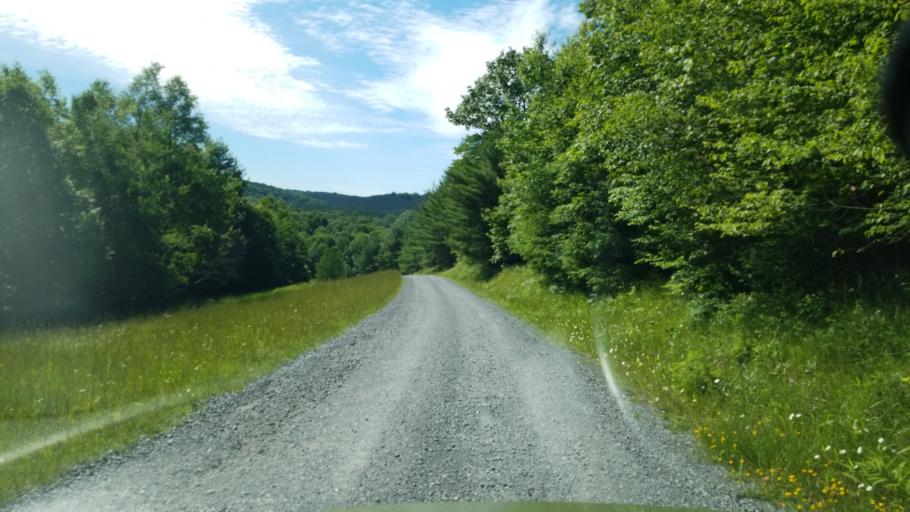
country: US
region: Pennsylvania
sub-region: Clearfield County
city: Clearfield
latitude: 41.2115
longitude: -78.4988
